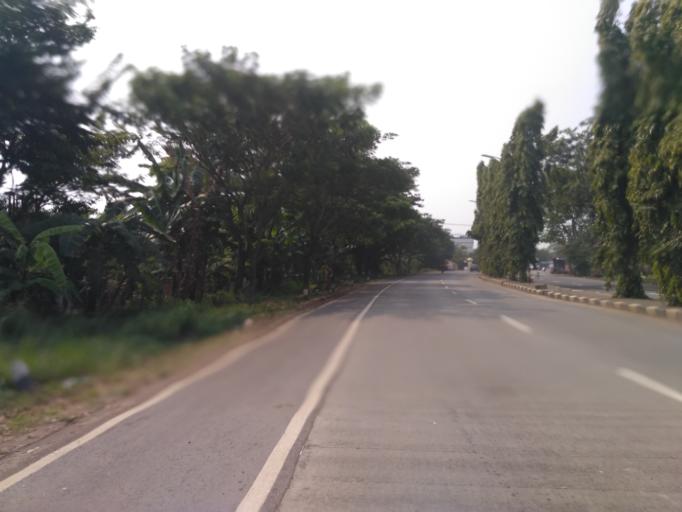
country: ID
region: Central Java
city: Semarang
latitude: -6.9741
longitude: 110.3877
